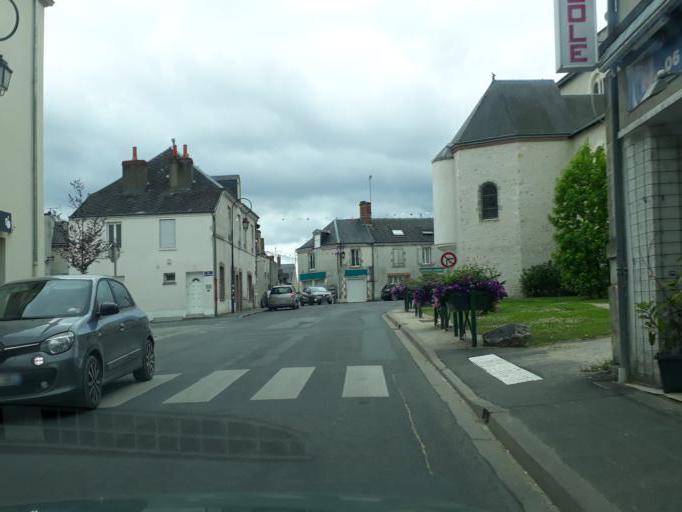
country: FR
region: Centre
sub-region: Departement du Loiret
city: Sandillon
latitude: 47.8460
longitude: 2.0333
